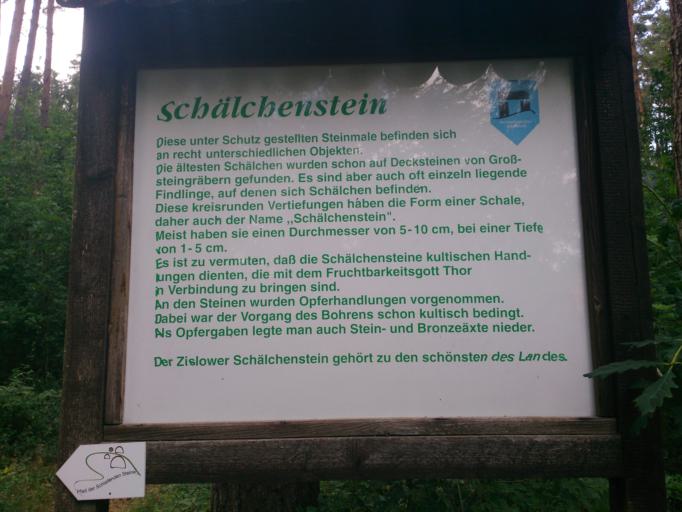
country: DE
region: Mecklenburg-Vorpommern
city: Plau am See
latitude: 53.4333
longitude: 12.3231
